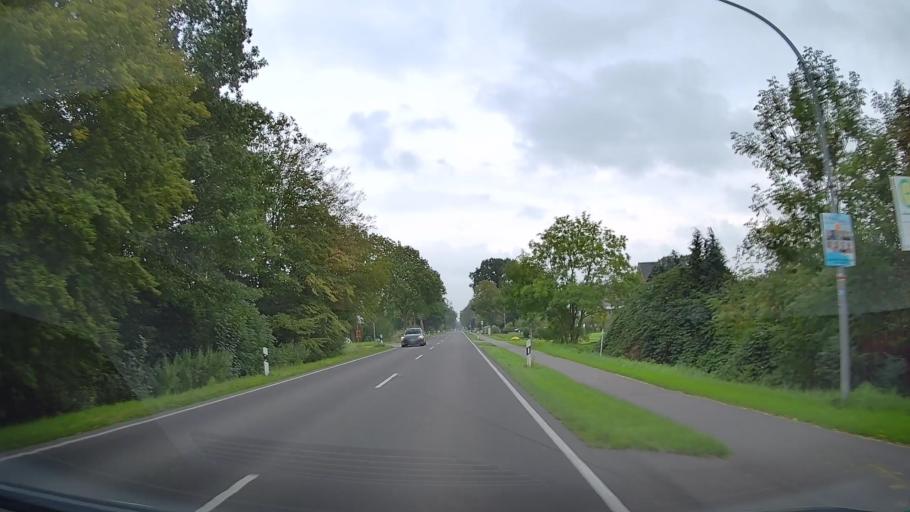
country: DE
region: Lower Saxony
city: Drochtersen
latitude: 53.7267
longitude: 9.3561
